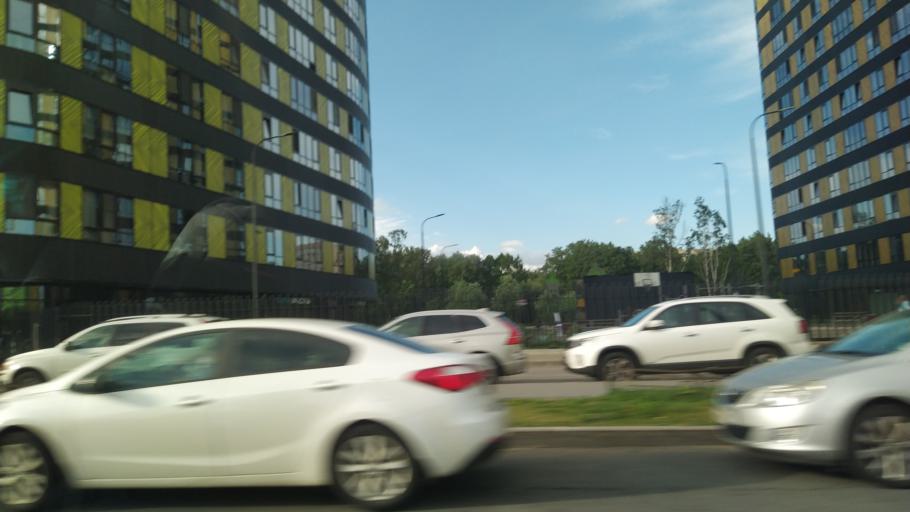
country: RU
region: Leningrad
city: Kalininskiy
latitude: 59.9628
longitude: 30.4018
